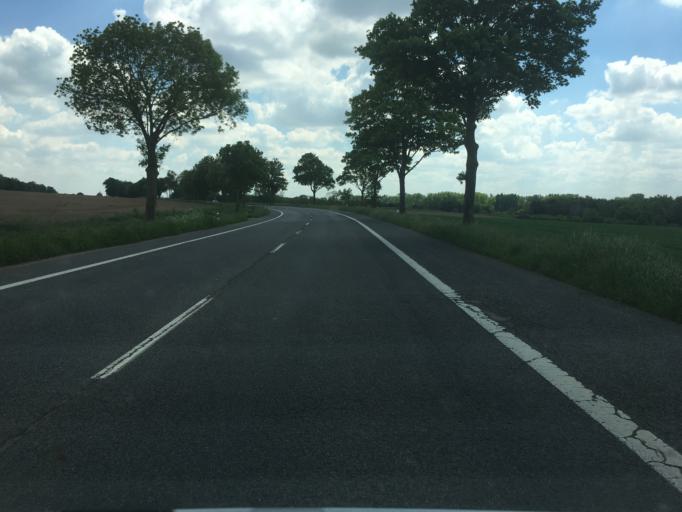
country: DE
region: North Rhine-Westphalia
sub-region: Regierungsbezirk Koln
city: Linnich
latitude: 50.9613
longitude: 6.3217
